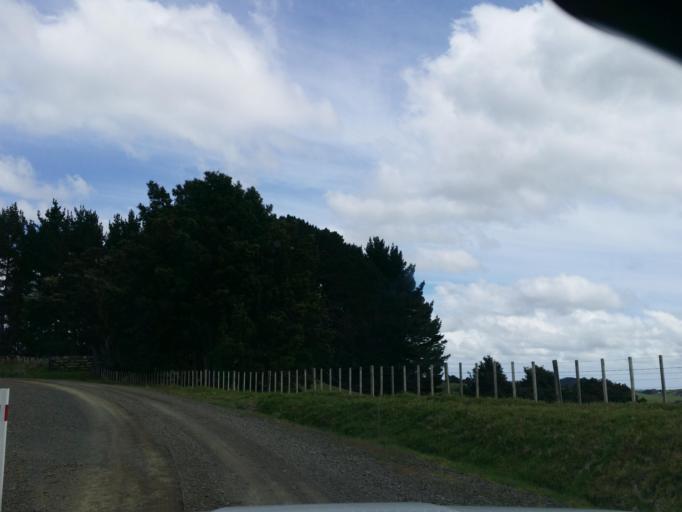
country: NZ
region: Northland
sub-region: Kaipara District
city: Dargaville
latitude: -35.9183
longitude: 174.0199
